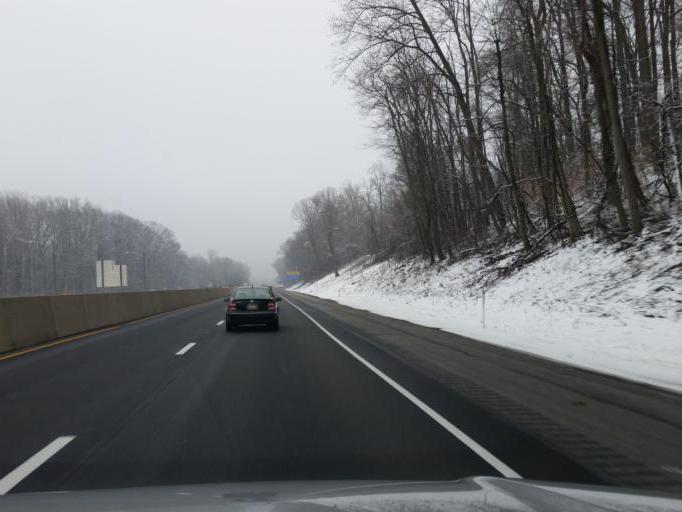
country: US
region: Pennsylvania
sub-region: York County
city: Valley Green
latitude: 40.1400
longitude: -76.8077
